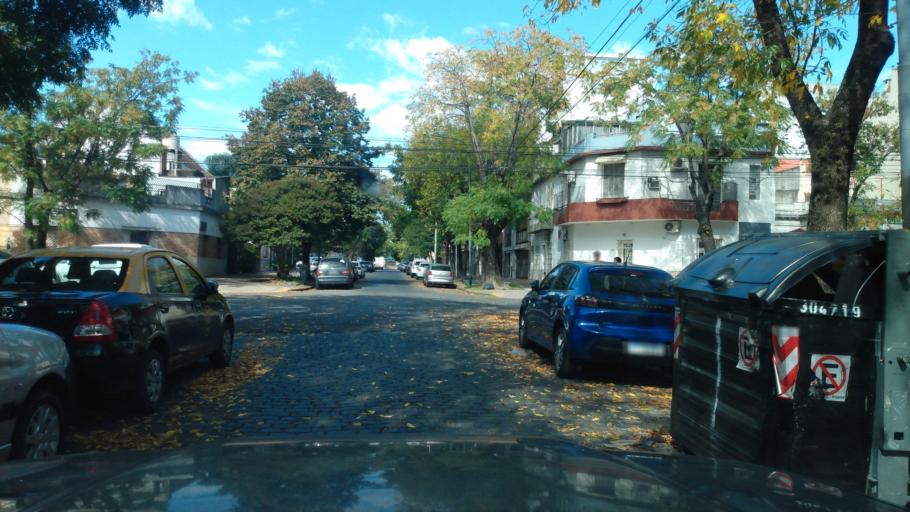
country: AR
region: Buenos Aires
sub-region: Partido de General San Martin
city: General San Martin
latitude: -34.5743
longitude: -58.4930
